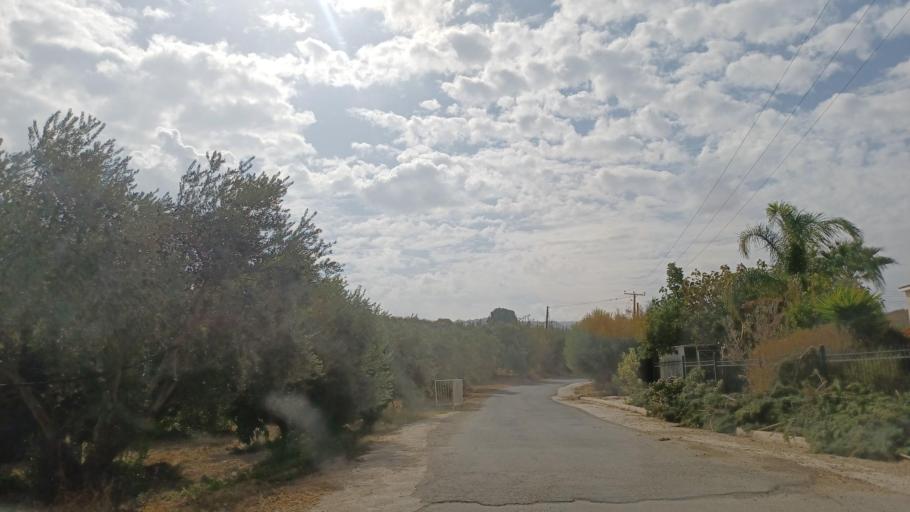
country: CY
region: Pafos
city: Polis
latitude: 35.0241
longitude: 32.4190
